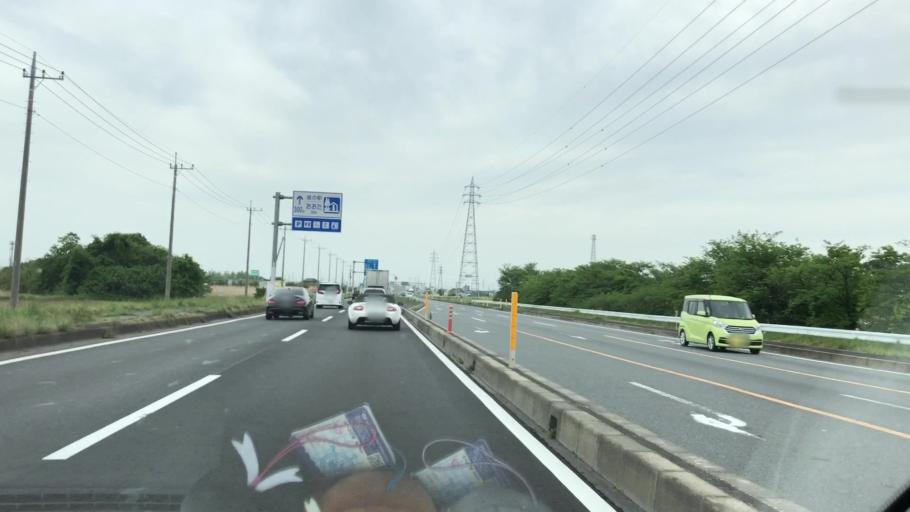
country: JP
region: Gunma
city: Sakai-nakajima
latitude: 36.2667
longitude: 139.2923
